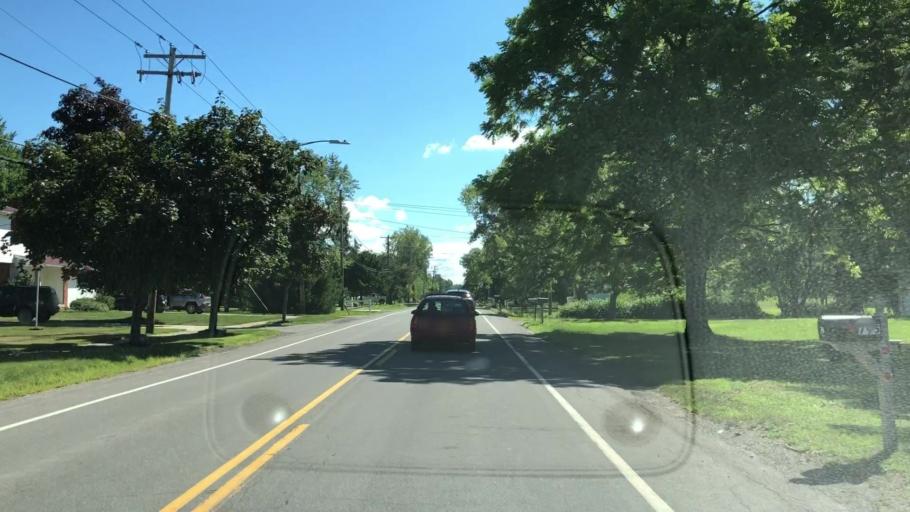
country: US
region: New York
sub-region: Erie County
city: Cheektowaga
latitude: 42.8509
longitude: -78.7249
